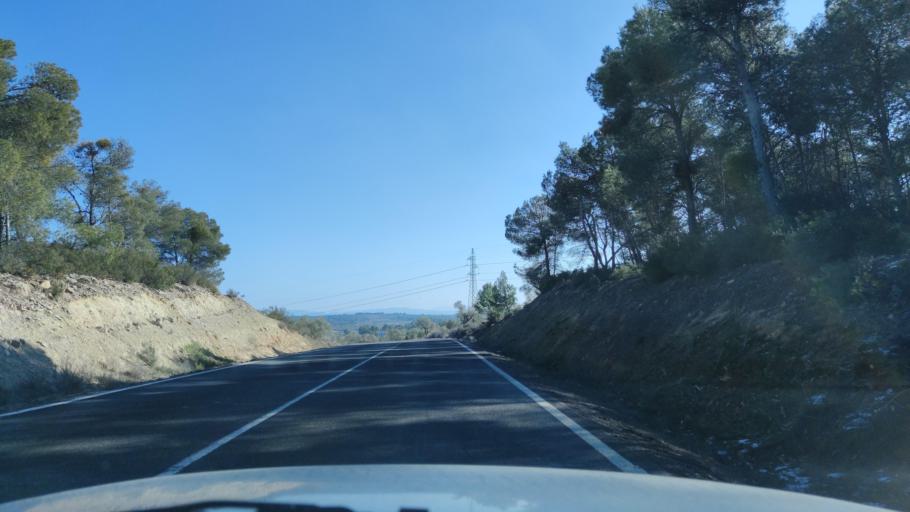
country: ES
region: Catalonia
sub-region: Provincia de Lleida
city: Maials
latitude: 41.3368
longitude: 0.4575
